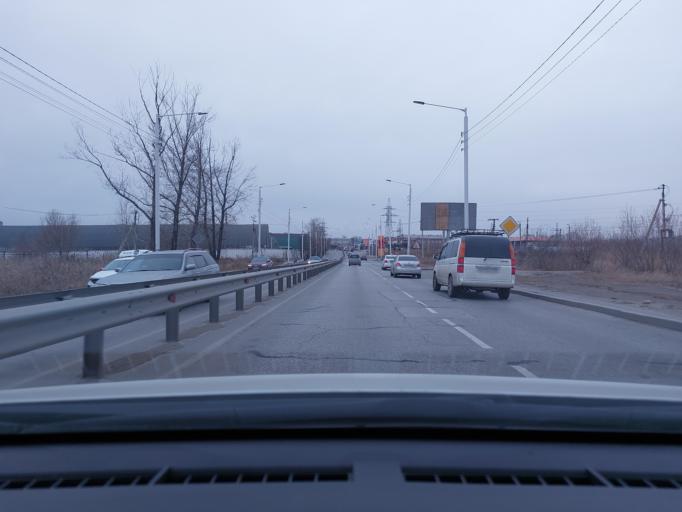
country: RU
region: Irkutsk
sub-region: Irkutskiy Rayon
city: Irkutsk
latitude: 52.3346
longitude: 104.2333
